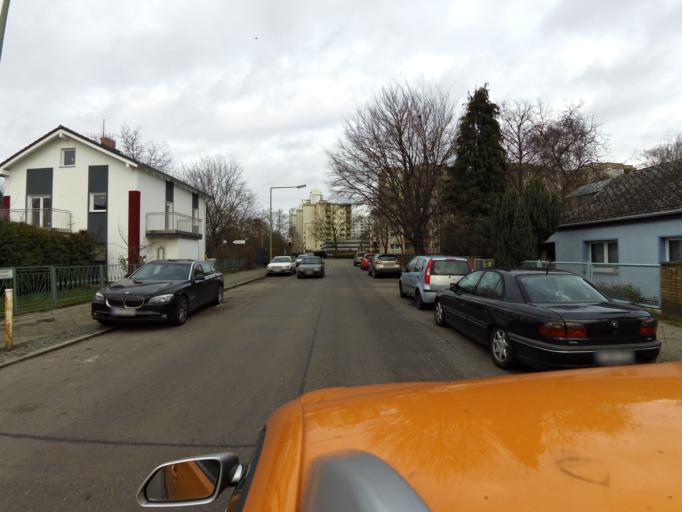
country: DE
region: Berlin
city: Gropiusstadt
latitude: 52.4192
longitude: 13.4737
